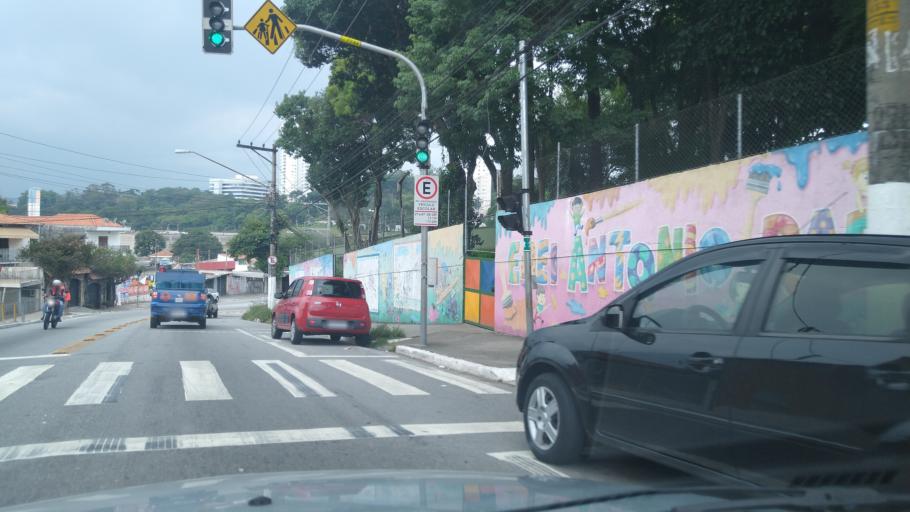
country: BR
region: Sao Paulo
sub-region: Osasco
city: Osasco
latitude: -23.5027
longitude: -46.7571
